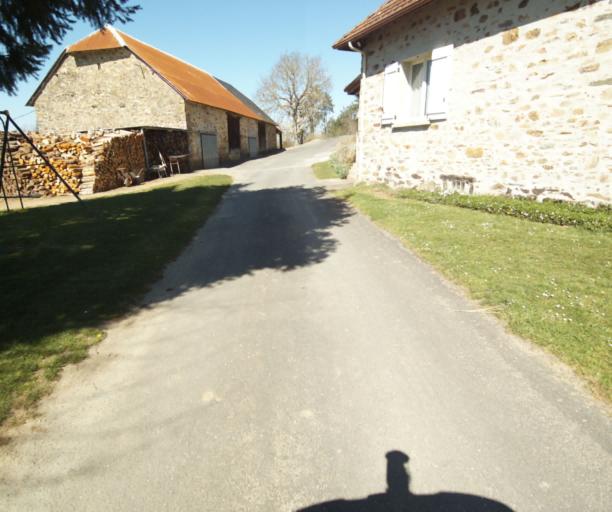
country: FR
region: Limousin
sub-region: Departement de la Correze
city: Chameyrat
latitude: 45.2731
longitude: 1.7115
